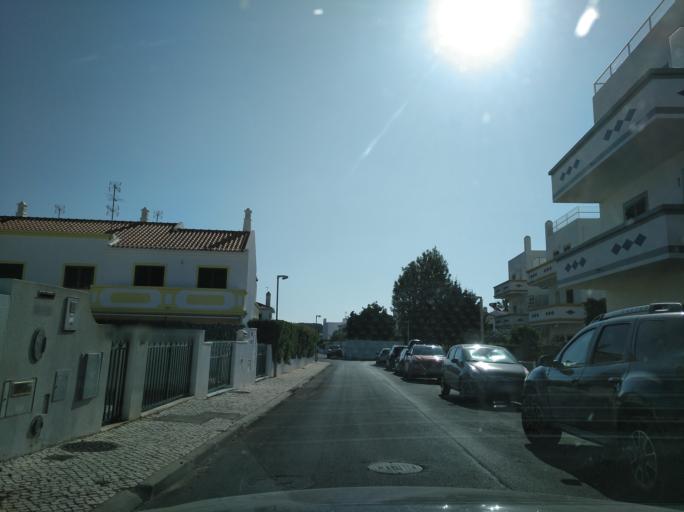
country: PT
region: Faro
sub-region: Vila Real de Santo Antonio
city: Monte Gordo
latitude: 37.1784
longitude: -7.4995
